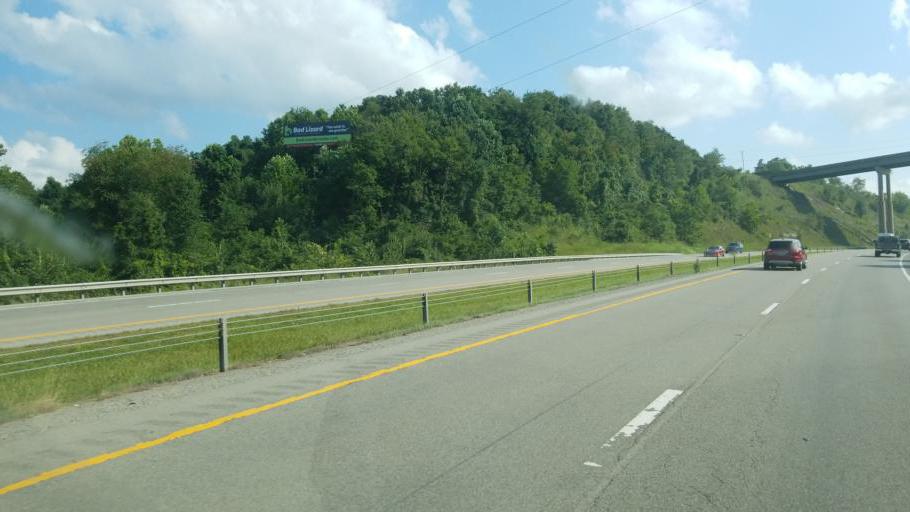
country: US
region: West Virginia
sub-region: Monongalia County
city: Brookhaven
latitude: 39.5950
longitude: -79.9304
